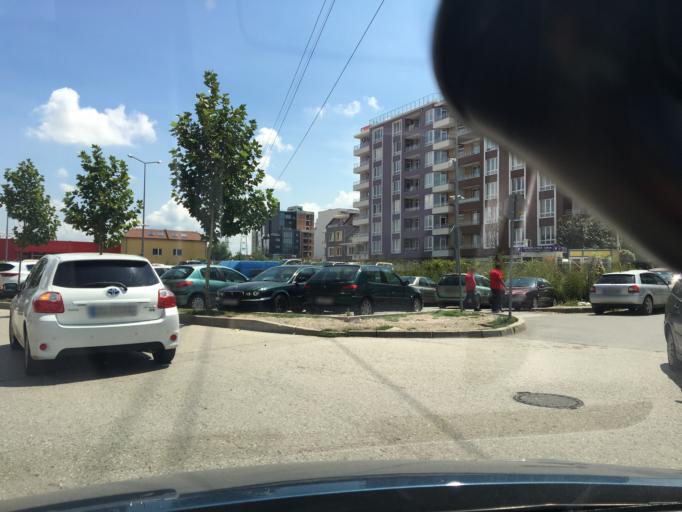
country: BG
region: Sofia-Capital
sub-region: Stolichna Obshtina
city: Sofia
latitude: 42.6570
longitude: 23.3127
